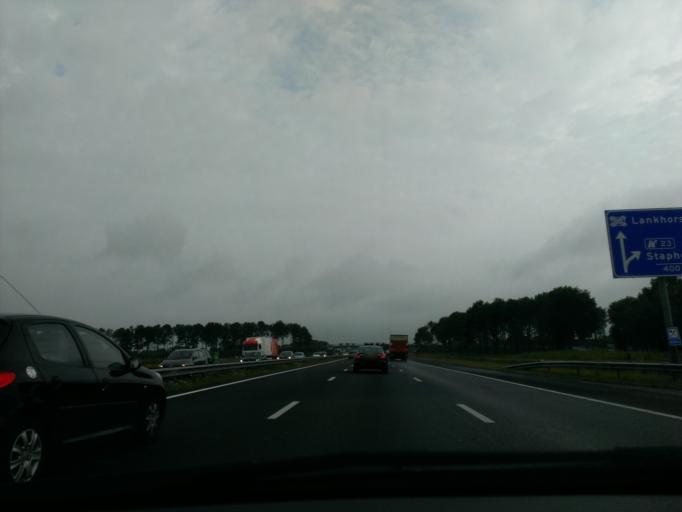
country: NL
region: Overijssel
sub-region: Gemeente Staphorst
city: Staphorst
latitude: 52.6312
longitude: 6.2054
